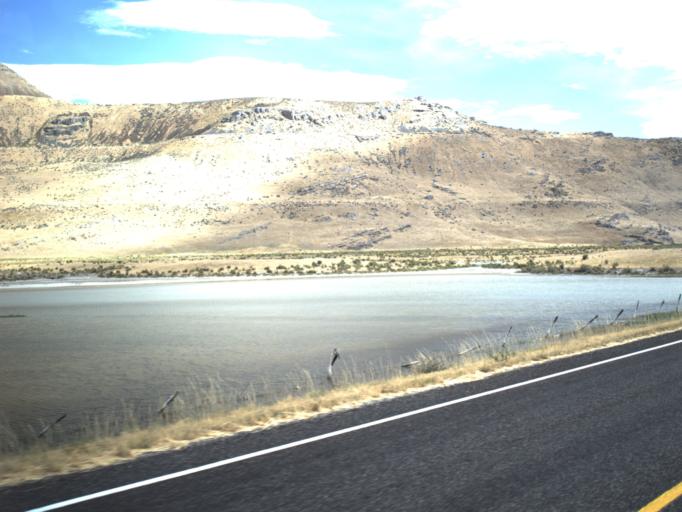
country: US
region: Utah
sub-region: Box Elder County
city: Tremonton
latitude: 41.5885
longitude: -112.2701
